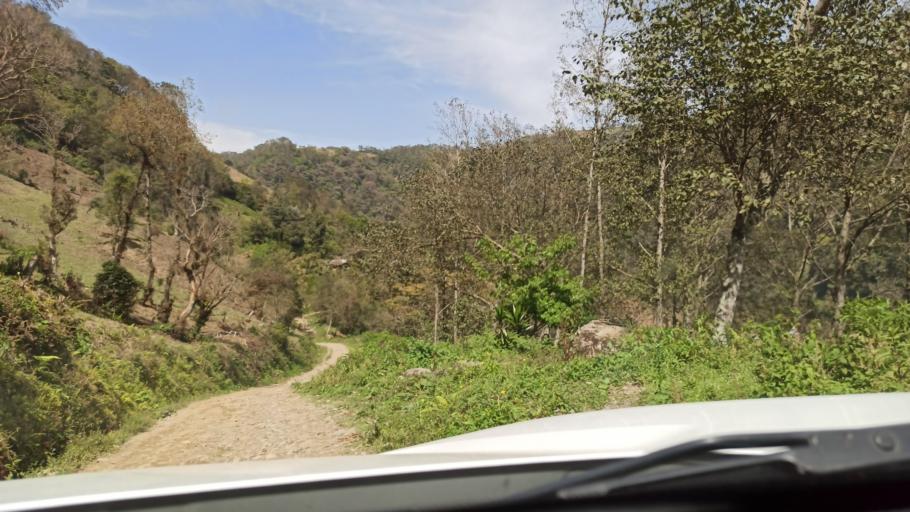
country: MX
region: Veracruz
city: Xocotla
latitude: 18.9839
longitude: -97.0985
